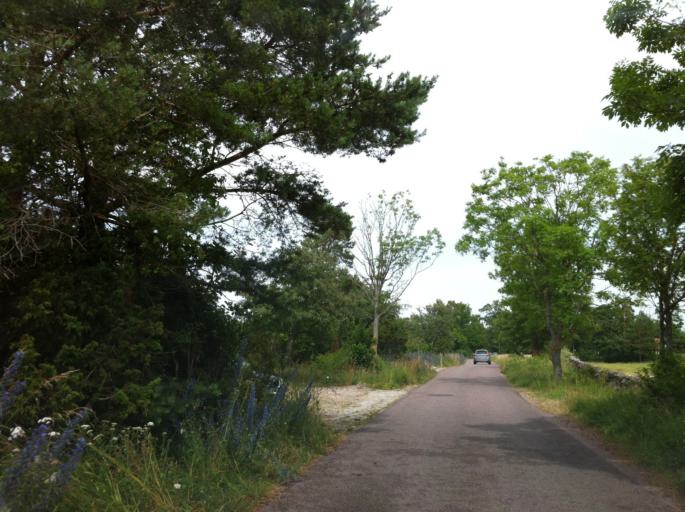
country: SE
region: Kalmar
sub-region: Oskarshamns Kommun
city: Oskarshamn
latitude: 57.3123
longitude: 16.9880
